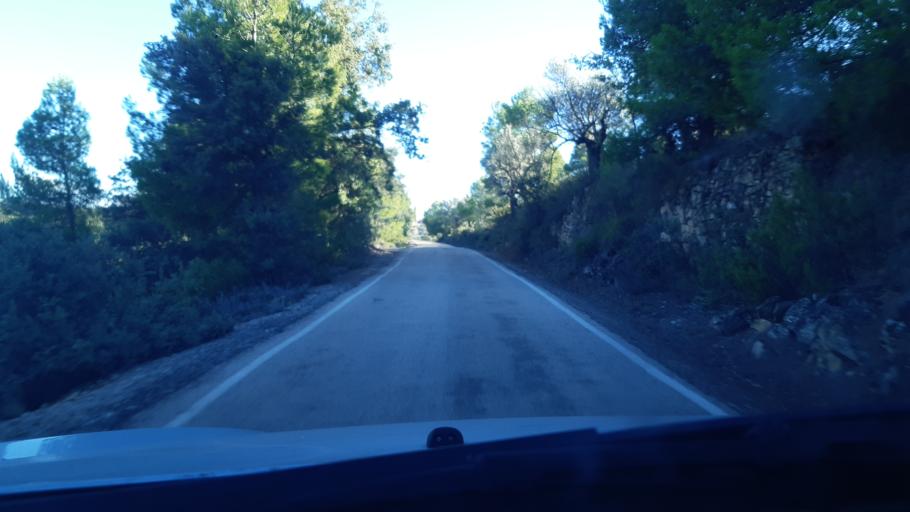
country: ES
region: Aragon
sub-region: Provincia de Teruel
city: Fornoles
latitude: 40.9055
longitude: -0.0117
